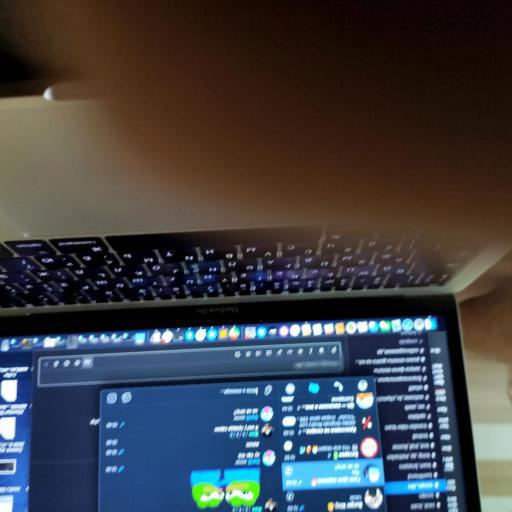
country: RU
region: Moscow
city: Mikhalkovo
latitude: 55.6703
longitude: 37.4247
